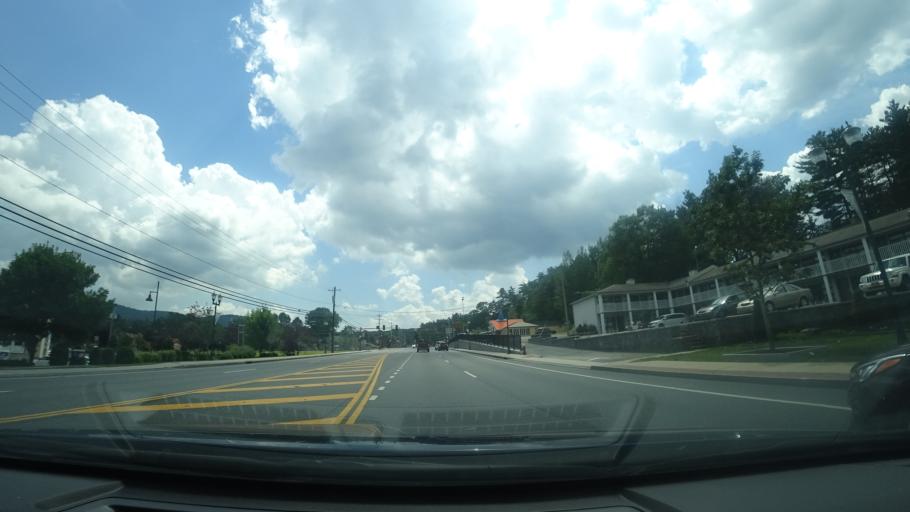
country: US
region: New York
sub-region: Warren County
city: Glens Falls North
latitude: 43.4108
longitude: -73.7112
